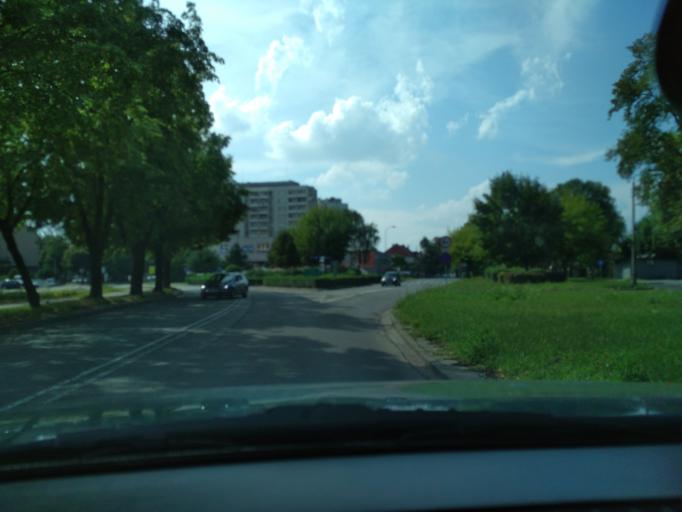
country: PL
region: Silesian Voivodeship
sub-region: Powiat raciborski
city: Raciborz
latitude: 50.0815
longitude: 18.2073
